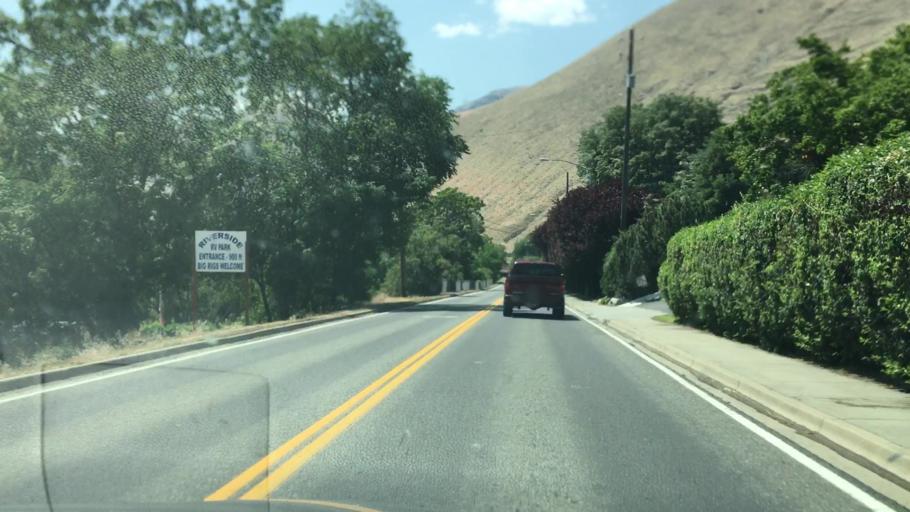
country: US
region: Idaho
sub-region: Idaho County
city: Grangeville
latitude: 45.4150
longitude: -116.3217
